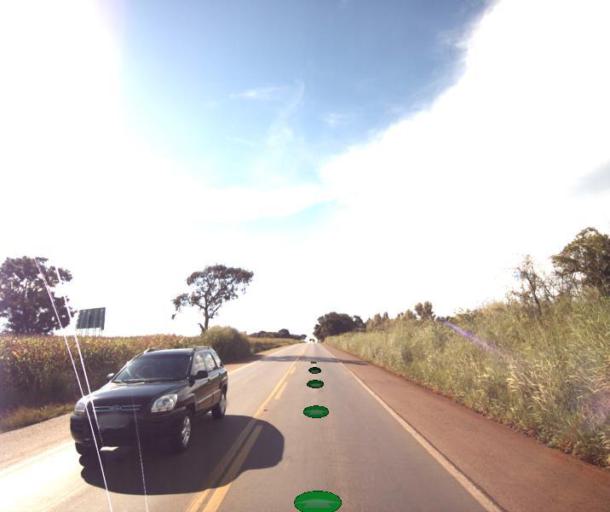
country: BR
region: Goias
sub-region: Rialma
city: Rialma
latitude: -15.3640
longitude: -49.5618
